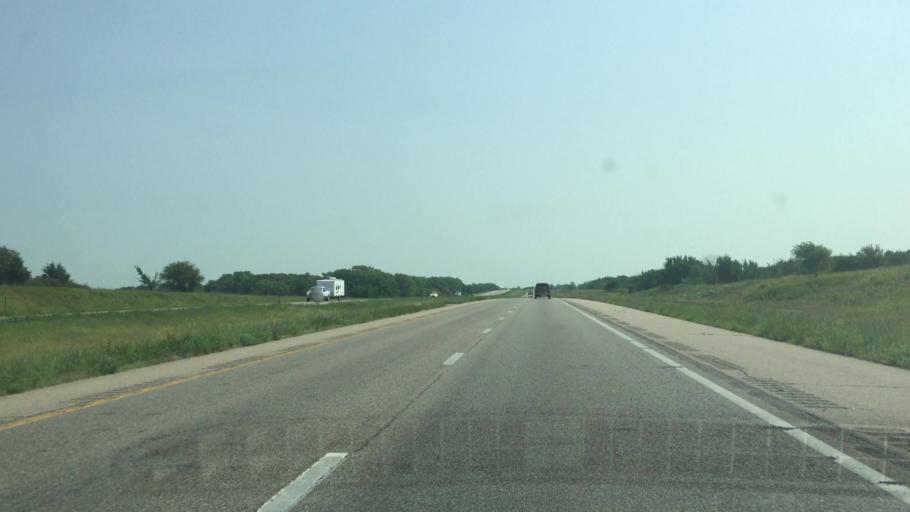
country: US
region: Kansas
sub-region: Osage County
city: Osage City
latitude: 38.4223
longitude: -95.9050
